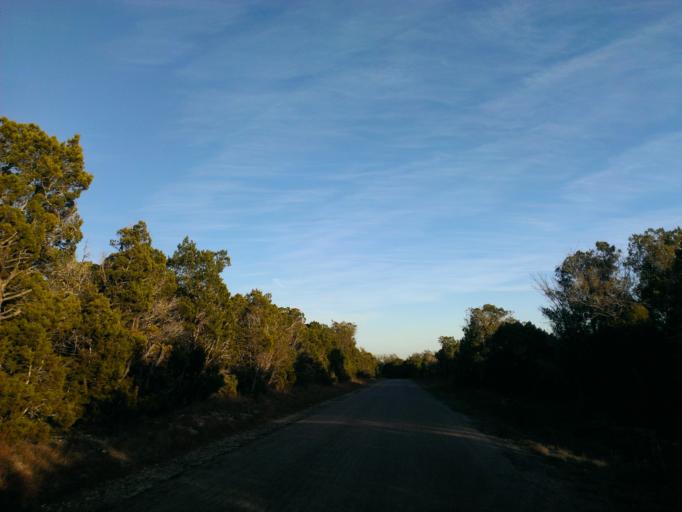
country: US
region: Texas
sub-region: Burnet County
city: Bertram
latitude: 30.7225
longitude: -98.0763
